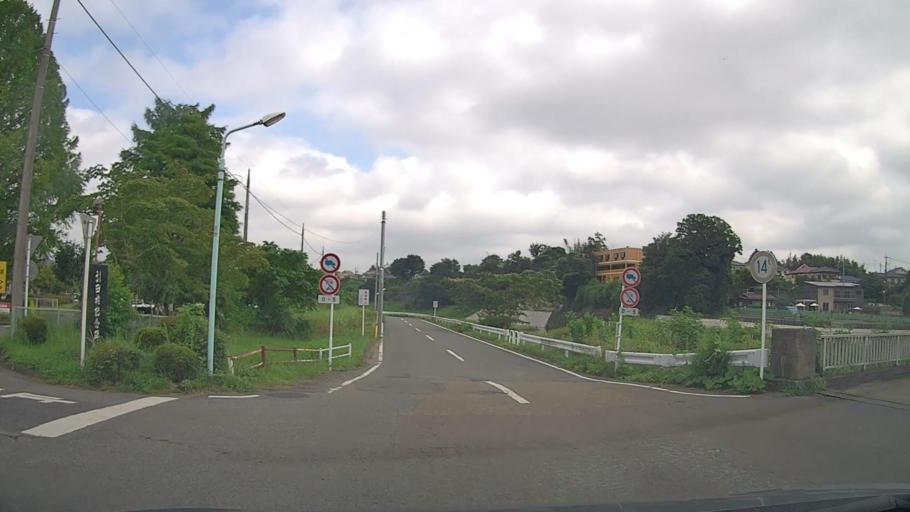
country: JP
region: Tokyo
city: Itsukaichi
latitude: 35.7198
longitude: 139.2632
